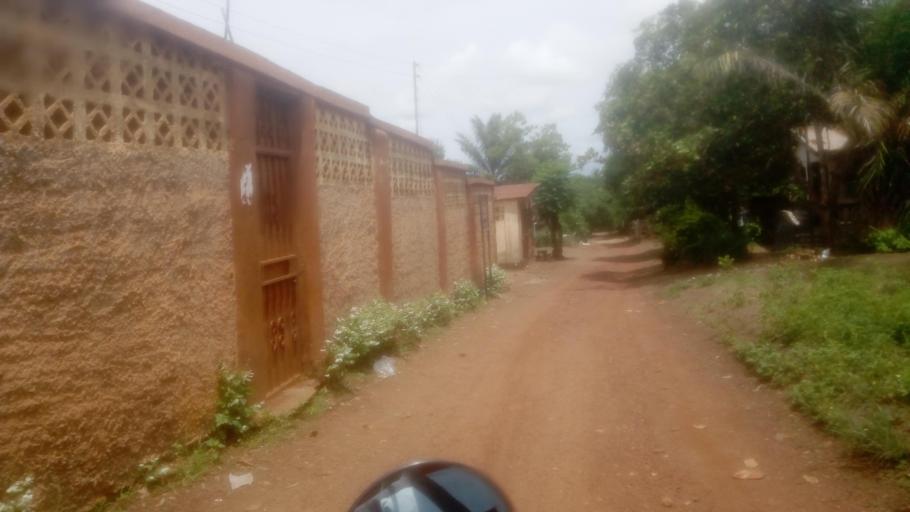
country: SL
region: Southern Province
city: Bo
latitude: 7.9551
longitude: -11.7128
